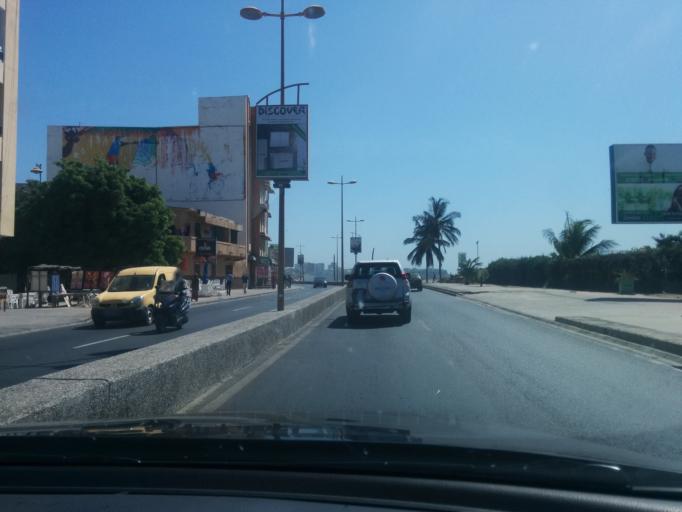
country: SN
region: Dakar
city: Dakar
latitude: 14.6752
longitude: -17.4533
